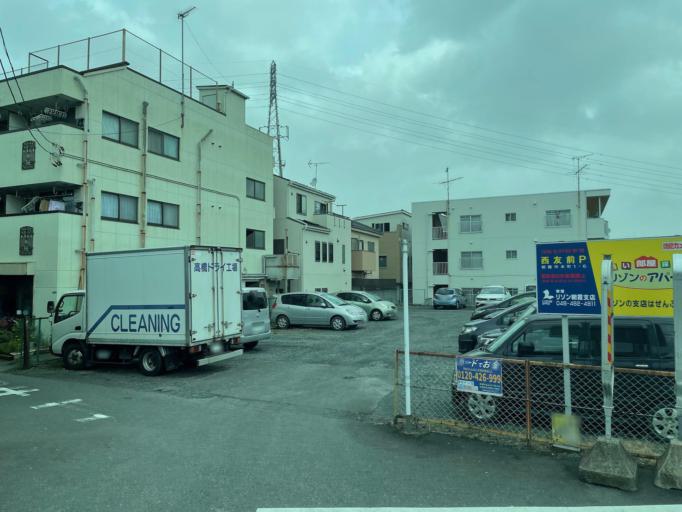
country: JP
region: Saitama
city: Asaka
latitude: 35.7979
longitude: 139.5916
